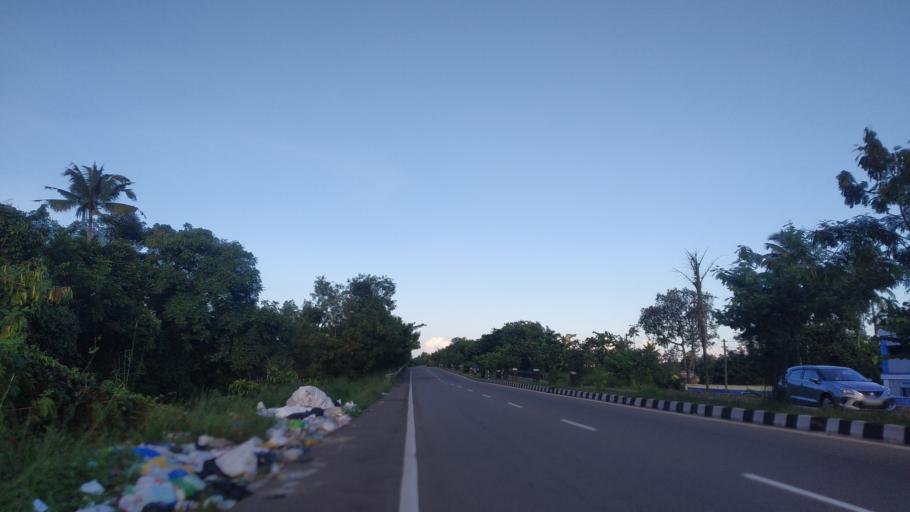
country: IN
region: Kerala
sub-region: Ernakulam
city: Elur
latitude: 10.0630
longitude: 76.2916
